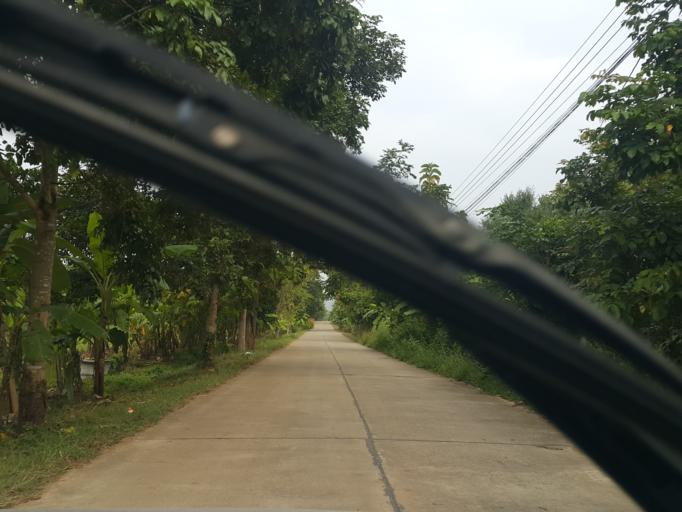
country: TH
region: Mae Hong Son
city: Wiang Nuea
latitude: 19.3705
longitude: 98.4485
